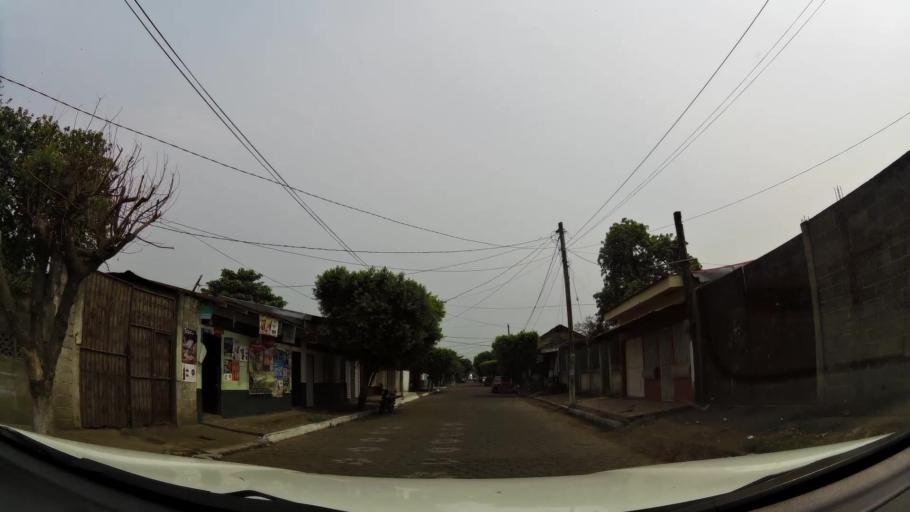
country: NI
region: Chinandega
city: Chinandega
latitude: 12.6257
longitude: -87.1364
